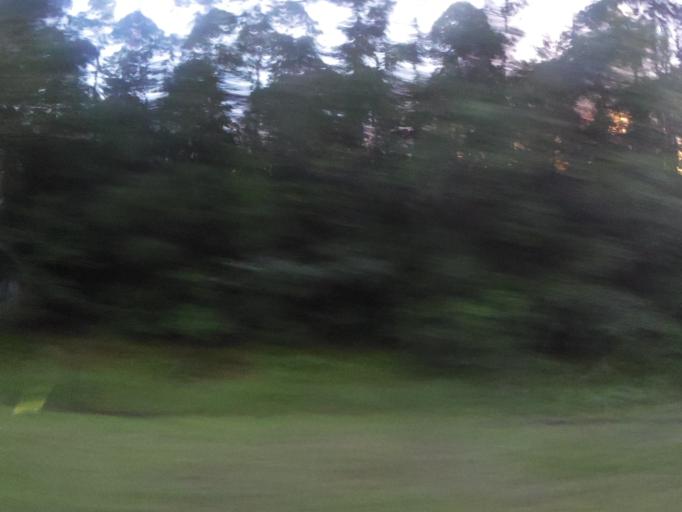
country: US
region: Georgia
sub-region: Camden County
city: Kingsland
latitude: 30.7650
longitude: -81.6889
